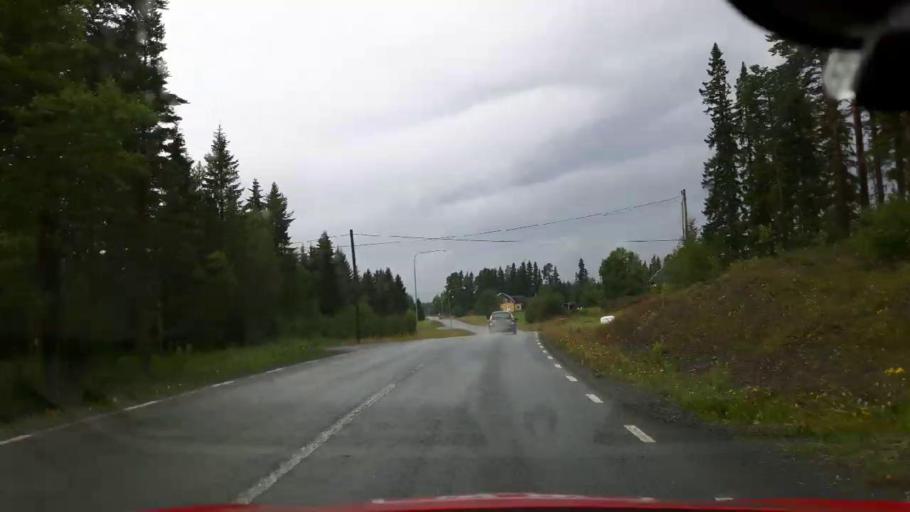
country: SE
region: Jaemtland
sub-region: Krokoms Kommun
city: Krokom
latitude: 63.3516
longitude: 14.1696
